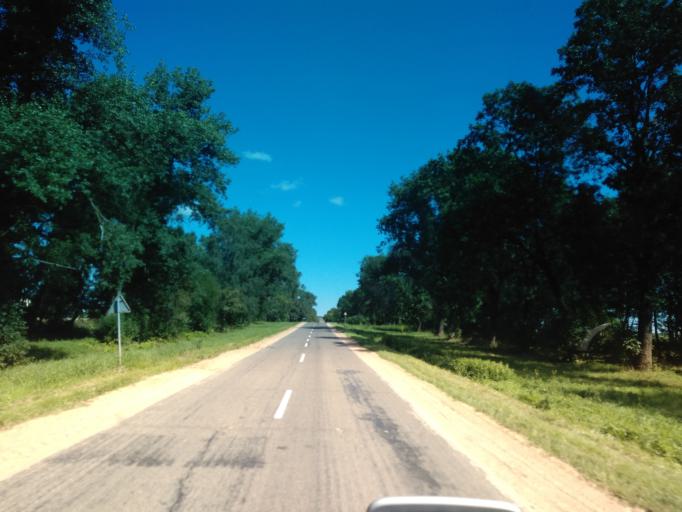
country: BY
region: Minsk
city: Stan'kava
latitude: 53.6320
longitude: 27.2740
